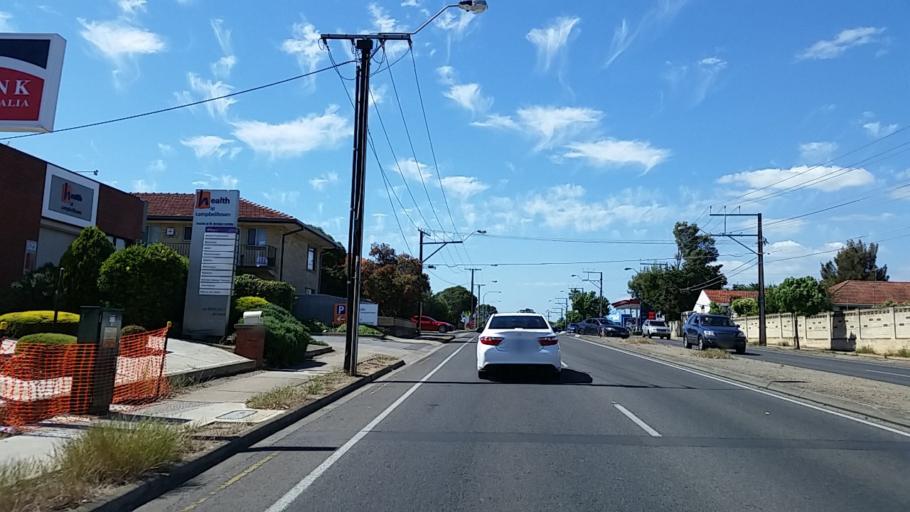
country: AU
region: South Australia
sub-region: Campbelltown
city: Hectorville
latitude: -34.8867
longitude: 138.6582
